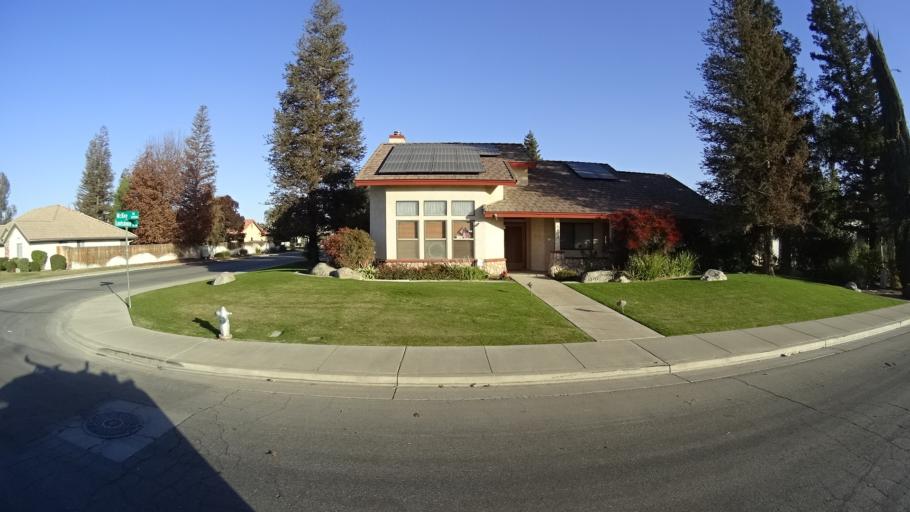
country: US
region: California
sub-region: Kern County
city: Greenfield
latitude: 35.2742
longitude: -119.0414
